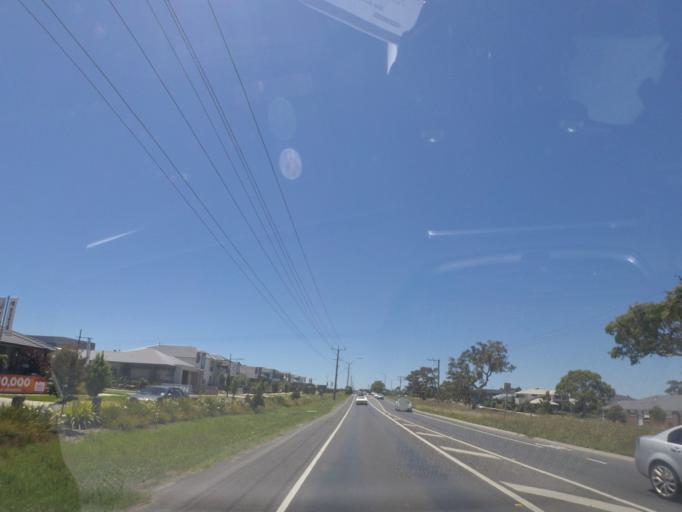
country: AU
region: Victoria
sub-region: Whittlesea
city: Epping
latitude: -37.6142
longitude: 145.0303
